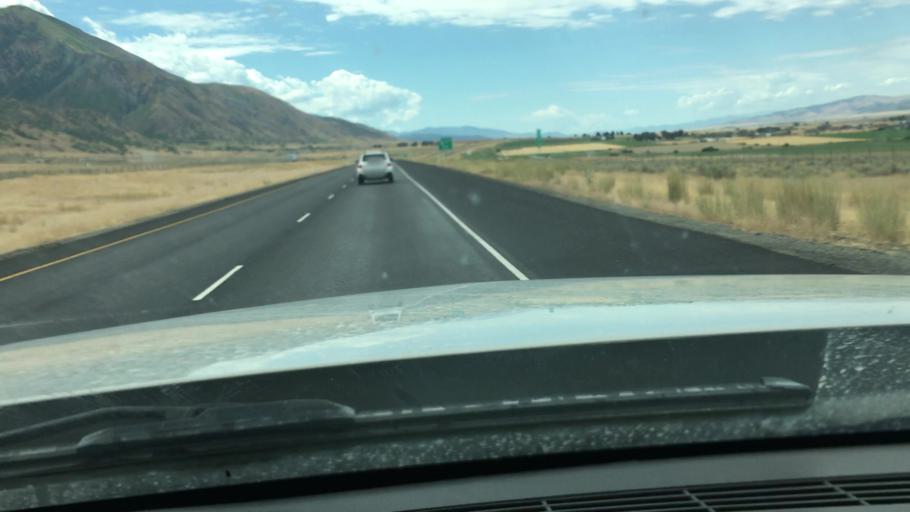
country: US
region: Utah
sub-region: Juab County
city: Mona
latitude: 39.8331
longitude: -111.8350
